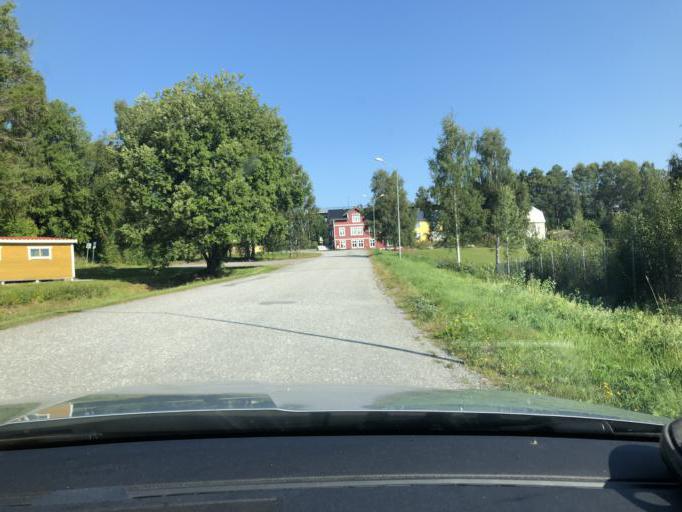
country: SE
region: Vaesternorrland
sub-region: Kramfors Kommun
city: Kramfors
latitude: 62.8801
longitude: 17.8728
